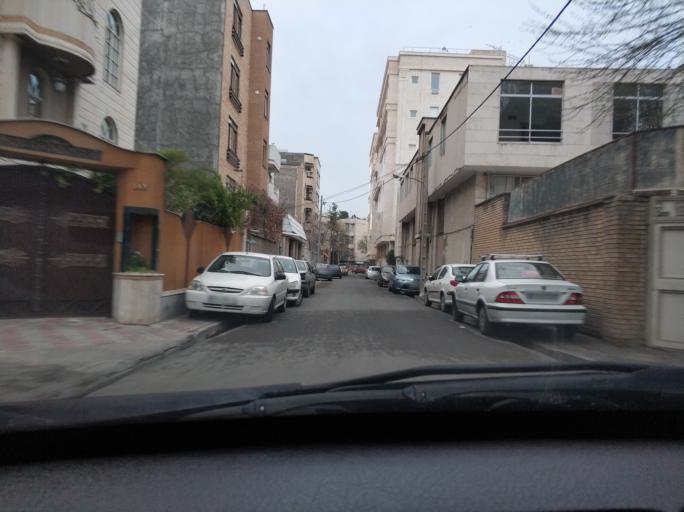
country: IR
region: Razavi Khorasan
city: Mashhad
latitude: 36.2747
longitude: 59.5936
